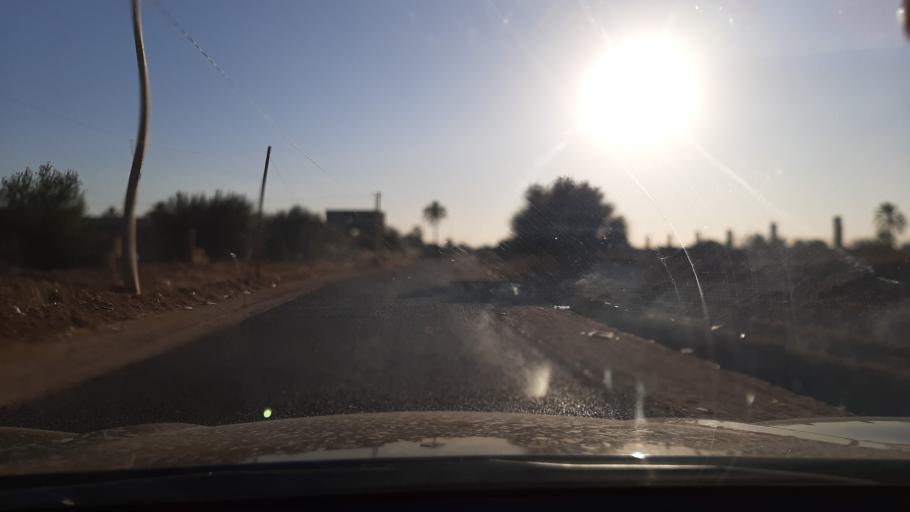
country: TN
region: Qabis
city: Matmata
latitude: 33.6177
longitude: 10.2643
